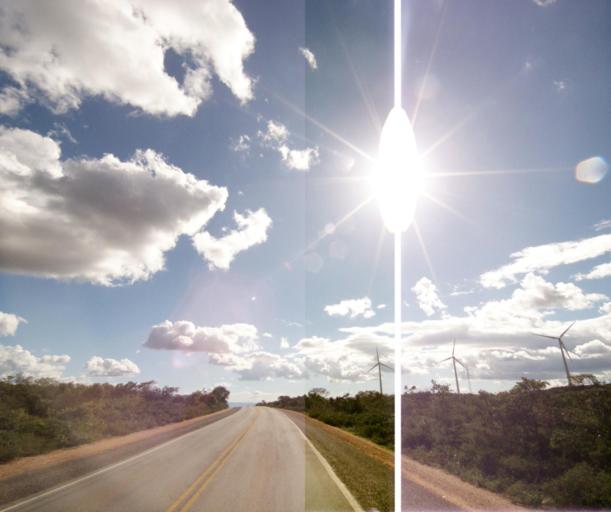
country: BR
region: Bahia
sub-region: Caetite
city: Caetite
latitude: -14.1173
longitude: -42.6063
